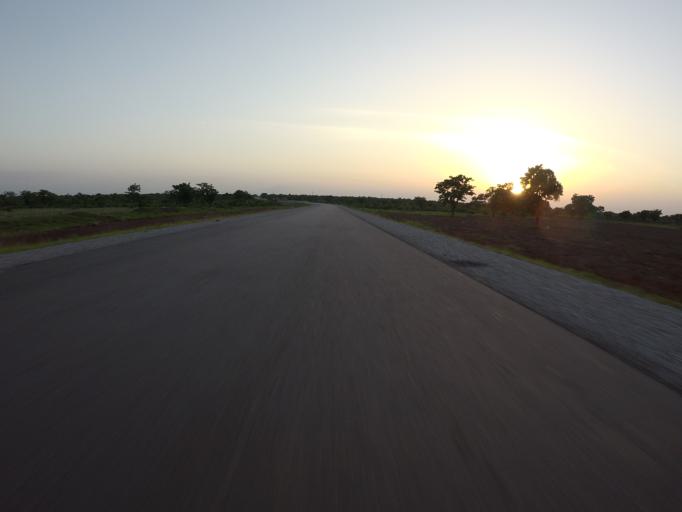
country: GH
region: Northern
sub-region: Yendi
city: Yendi
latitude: 9.9386
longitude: -0.1746
